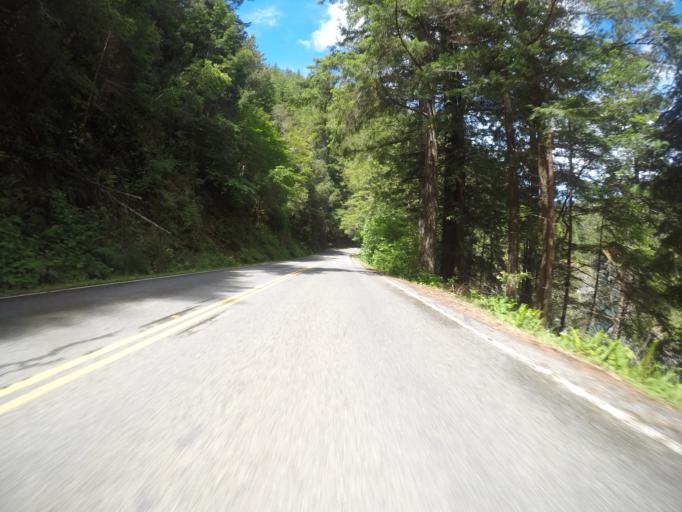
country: US
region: California
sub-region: Del Norte County
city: Bertsch-Oceanview
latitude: 41.7949
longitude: -124.0481
